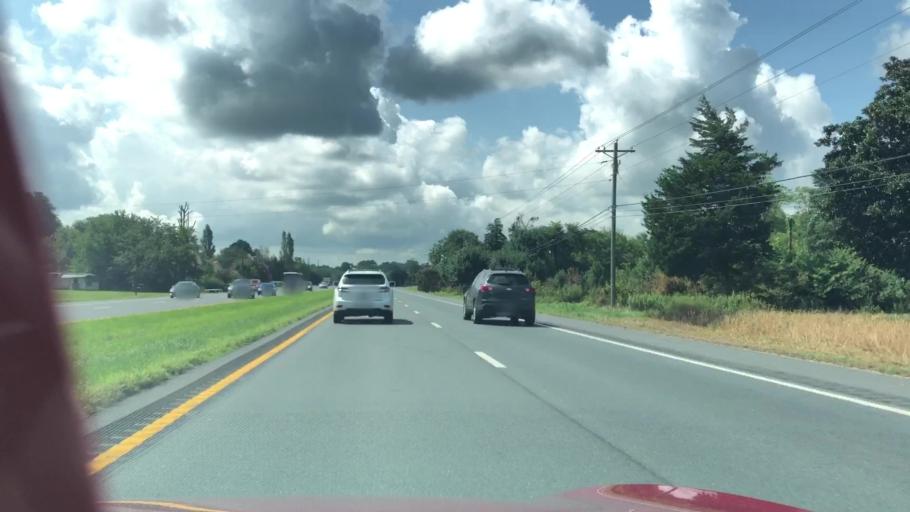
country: US
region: Virginia
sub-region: Accomack County
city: Accomac
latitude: 37.7774
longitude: -75.6114
